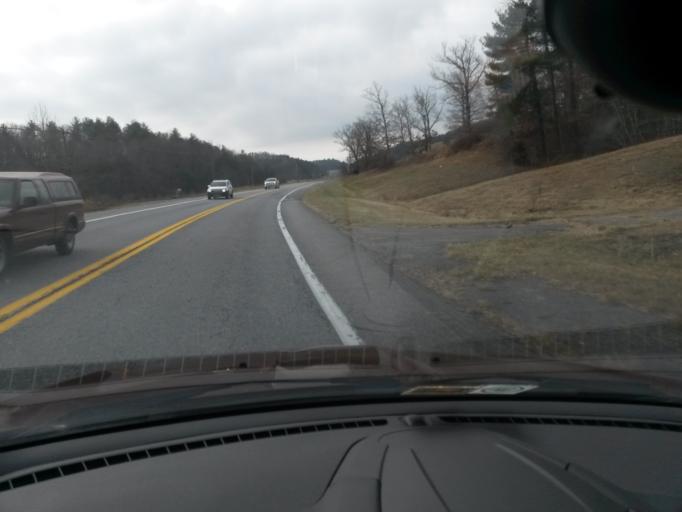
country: US
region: Virginia
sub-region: Alleghany County
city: Clifton Forge
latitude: 37.7527
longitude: -79.7875
